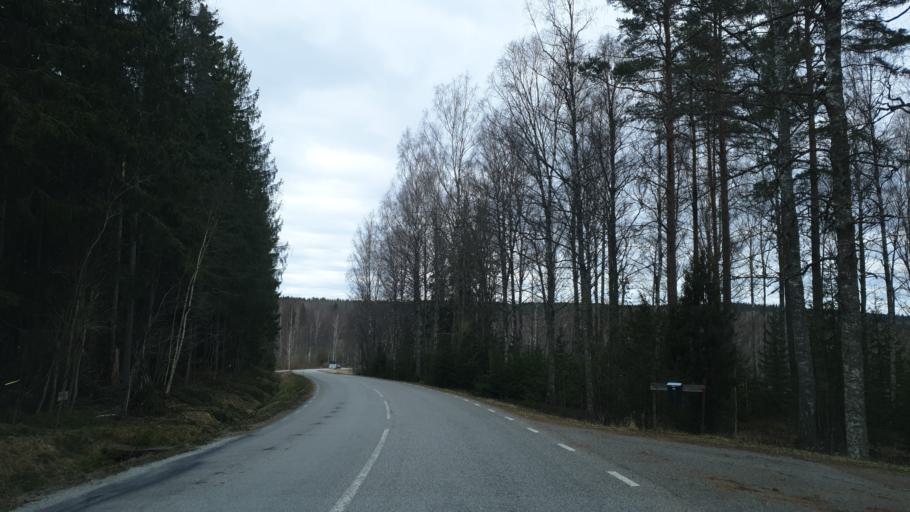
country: SE
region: OErebro
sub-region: Nora Kommun
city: As
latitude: 59.6012
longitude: 14.9345
